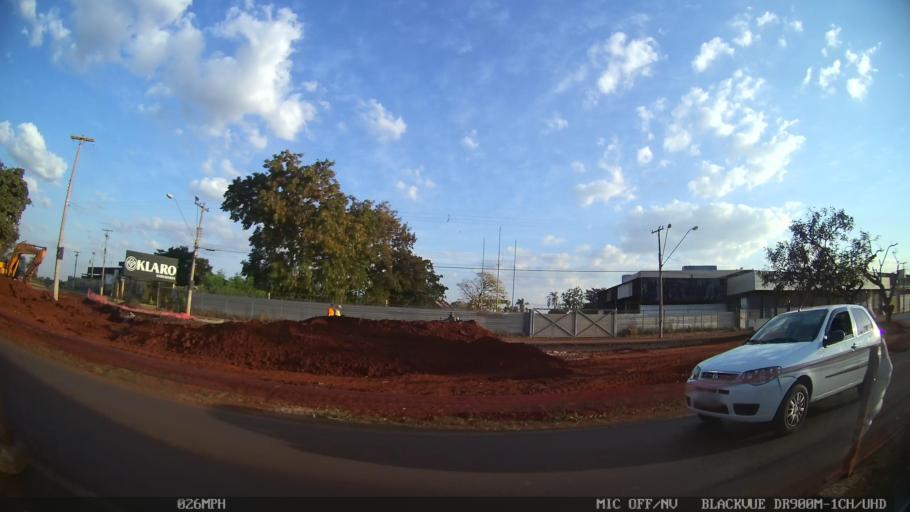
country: BR
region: Sao Paulo
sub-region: Ribeirao Preto
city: Ribeirao Preto
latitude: -21.1437
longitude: -47.7763
